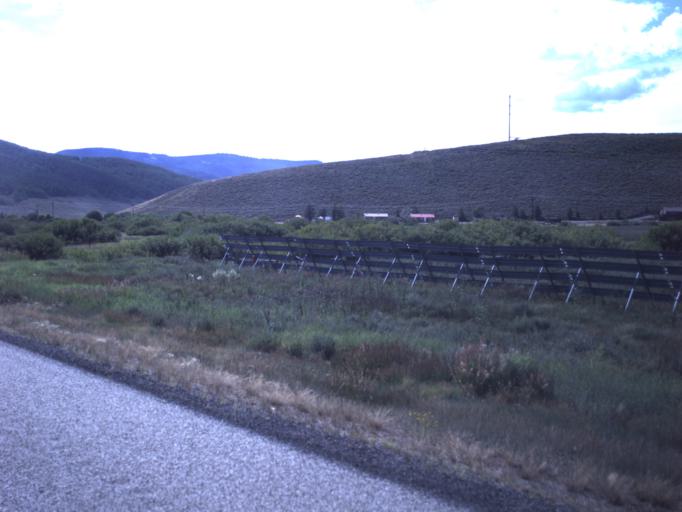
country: US
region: Utah
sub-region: Wasatch County
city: Heber
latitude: 40.2418
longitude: -111.1765
